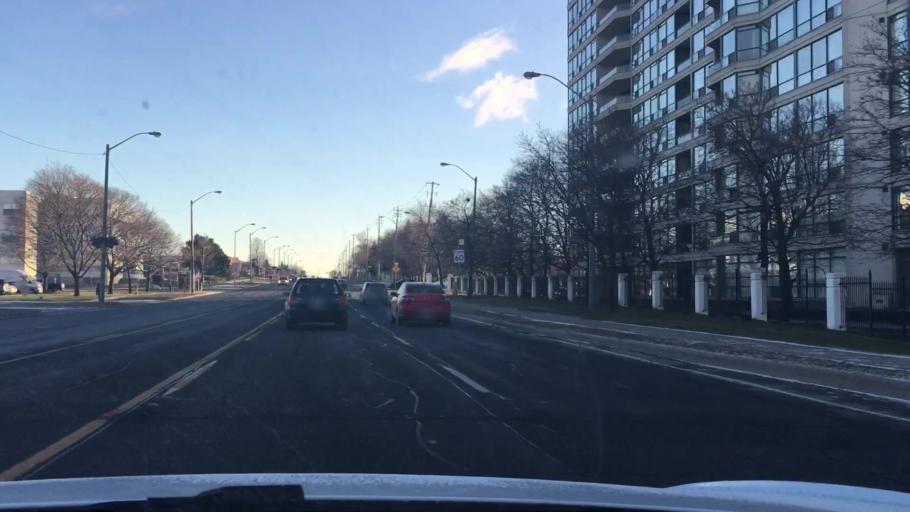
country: CA
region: Ontario
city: Scarborough
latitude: 43.7904
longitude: -79.2551
